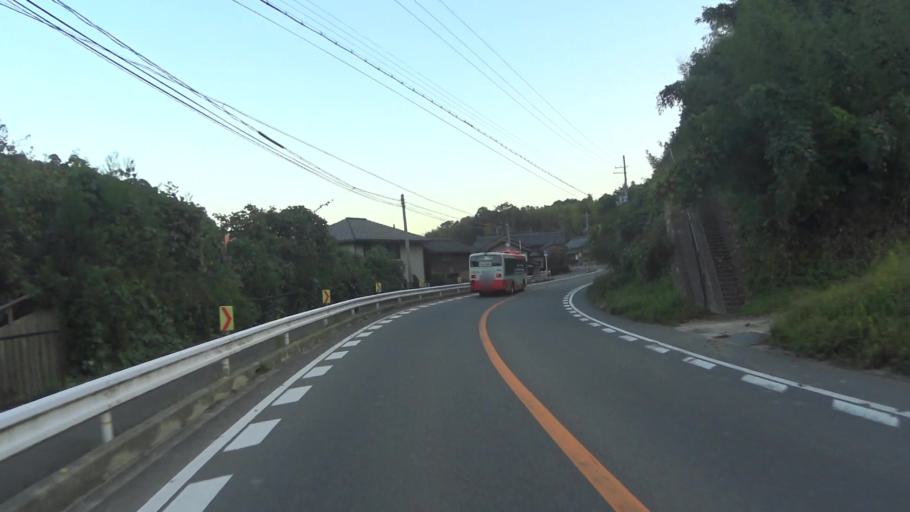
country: JP
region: Kyoto
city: Miyazu
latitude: 35.6416
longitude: 135.0522
